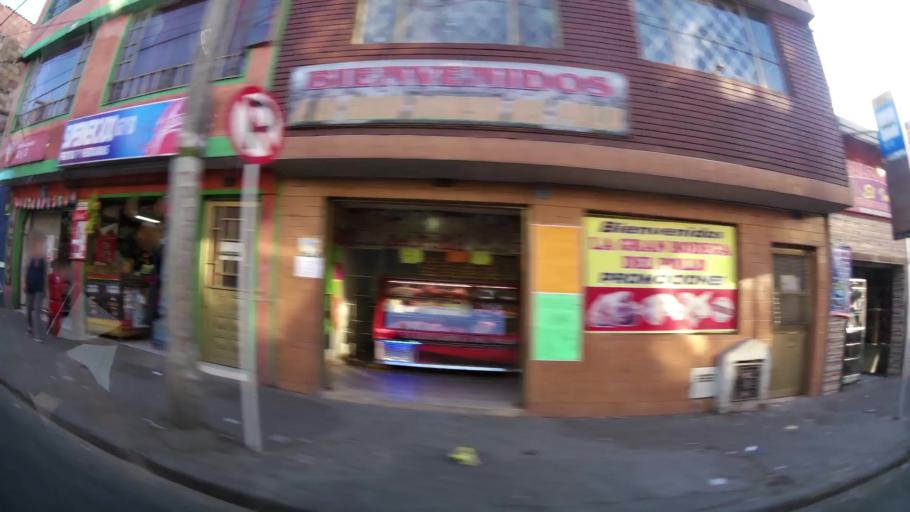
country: CO
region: Bogota D.C.
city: Bogota
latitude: 4.5657
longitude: -74.1311
